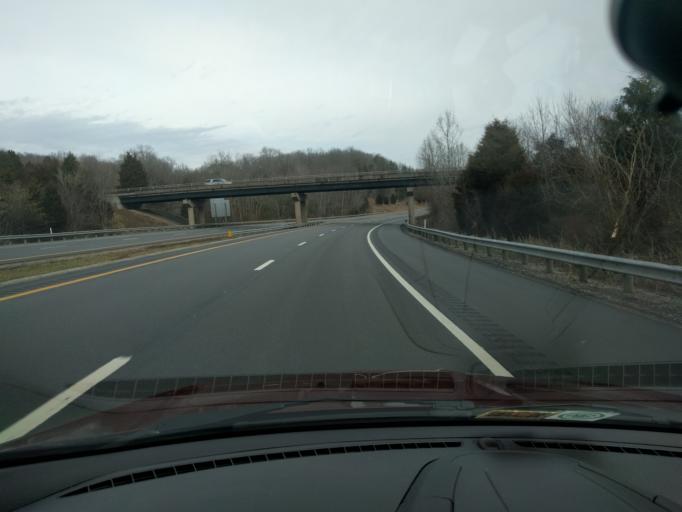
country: US
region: West Virginia
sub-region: Jackson County
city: Ripley
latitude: 38.7752
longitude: -81.7238
